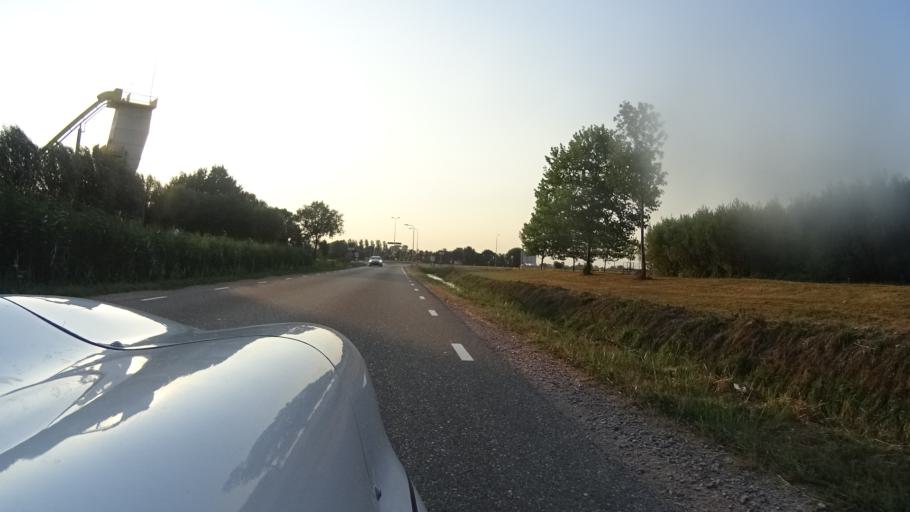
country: NL
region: Gelderland
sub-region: Gemeente Tiel
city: Tiel
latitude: 51.9285
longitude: 5.4356
